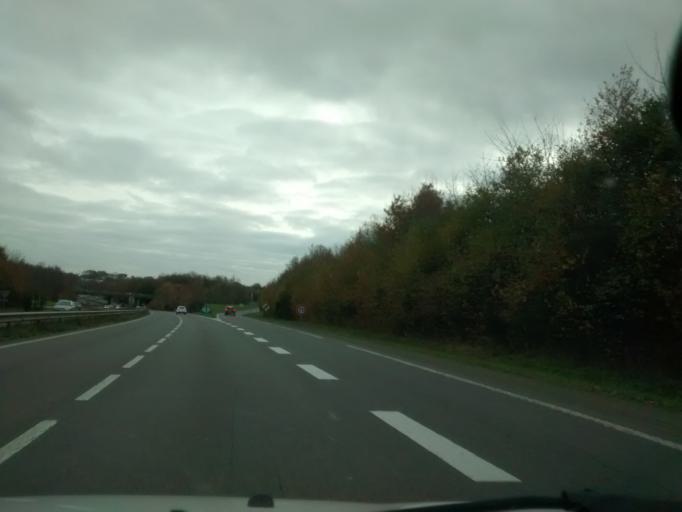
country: FR
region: Brittany
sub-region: Departement d'Ille-et-Vilaine
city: La Meziere
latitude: 48.2072
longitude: -1.7363
